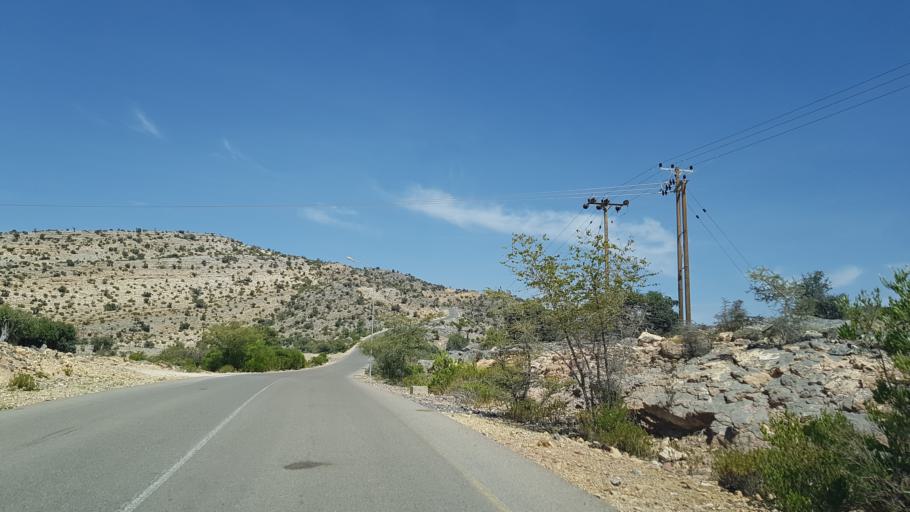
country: OM
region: Al Batinah
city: Bayt al `Awabi
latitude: 23.1352
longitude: 57.5587
